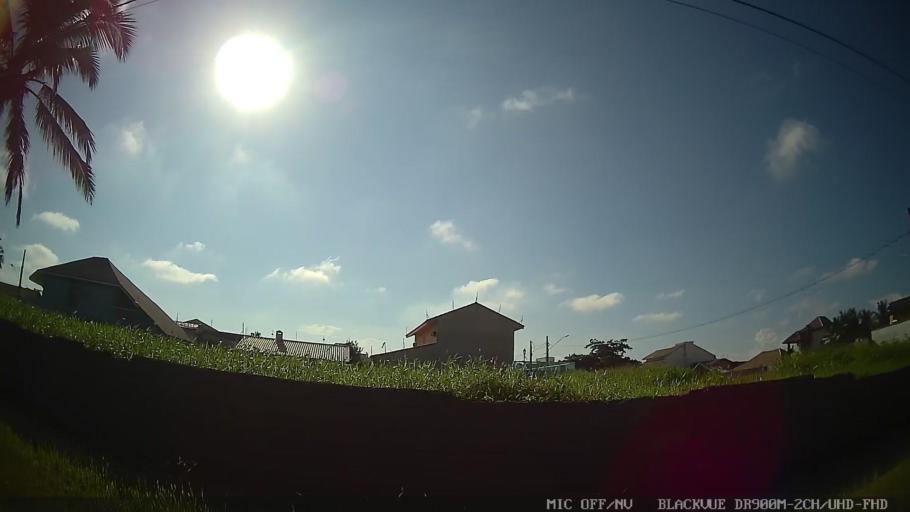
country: BR
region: Sao Paulo
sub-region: Peruibe
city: Peruibe
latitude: -24.2884
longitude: -46.9532
